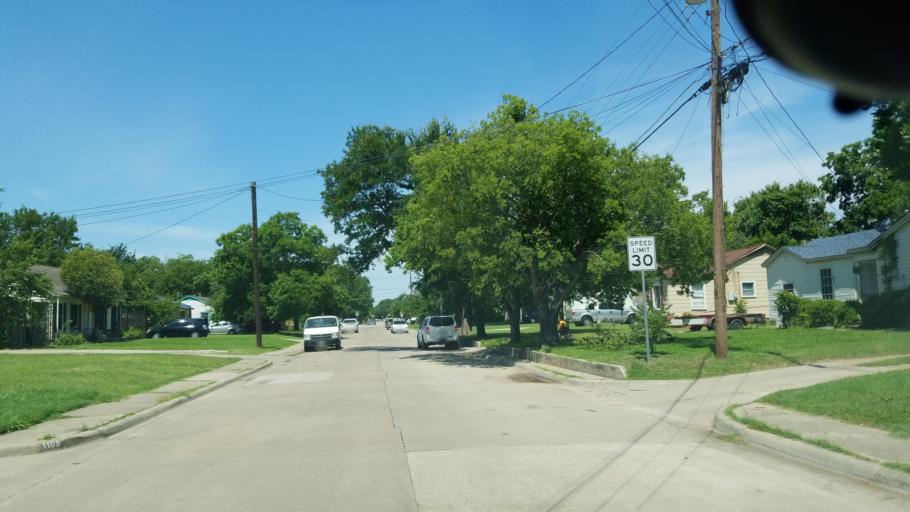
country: US
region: Texas
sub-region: Dallas County
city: Irving
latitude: 32.8200
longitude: -96.9326
